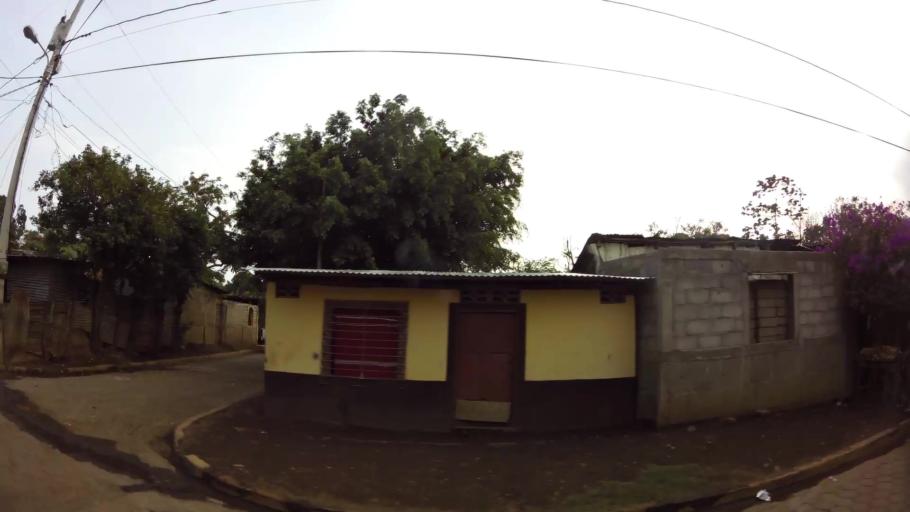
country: NI
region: Masaya
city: Masaya
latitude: 11.9830
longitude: -86.1039
